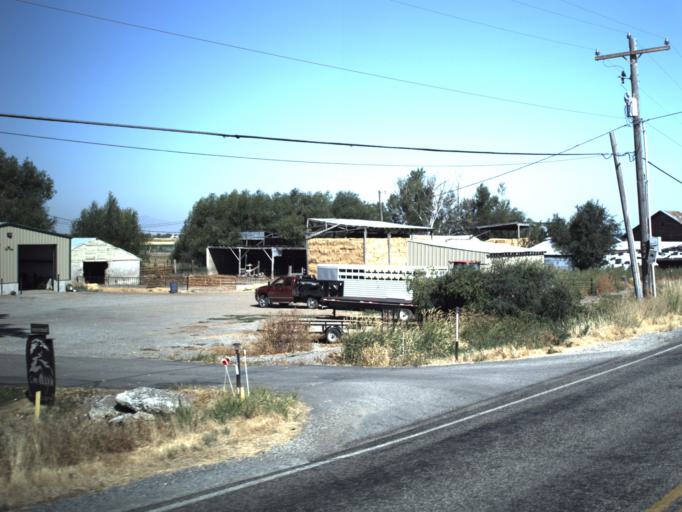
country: US
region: Utah
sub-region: Cache County
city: Hyrum
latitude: 41.5966
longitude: -111.8352
